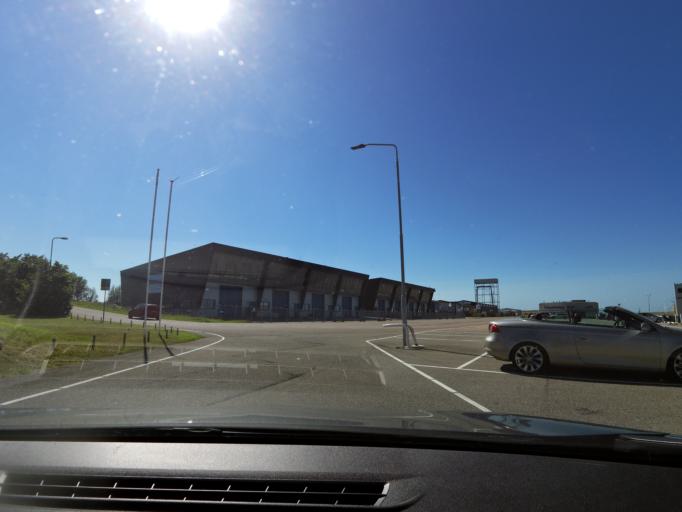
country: NL
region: South Holland
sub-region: Gemeente Goeree-Overflakkee
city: Goedereede
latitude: 51.8239
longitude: 4.0347
